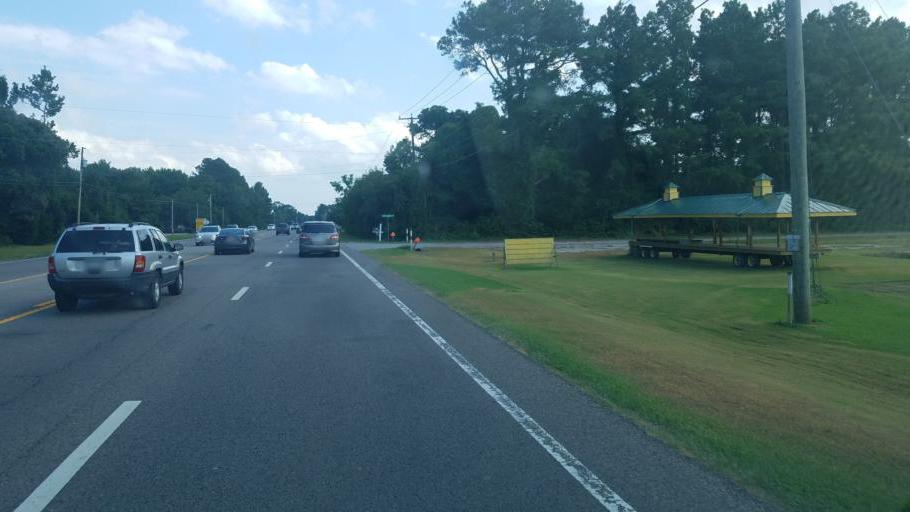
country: US
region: North Carolina
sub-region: Dare County
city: Southern Shores
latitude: 36.2546
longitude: -75.8926
